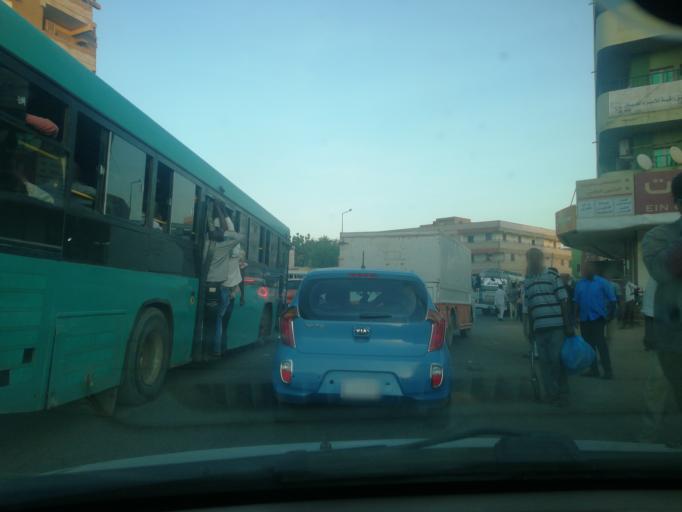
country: SD
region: Khartoum
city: Khartoum
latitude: 15.6241
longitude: 32.5561
